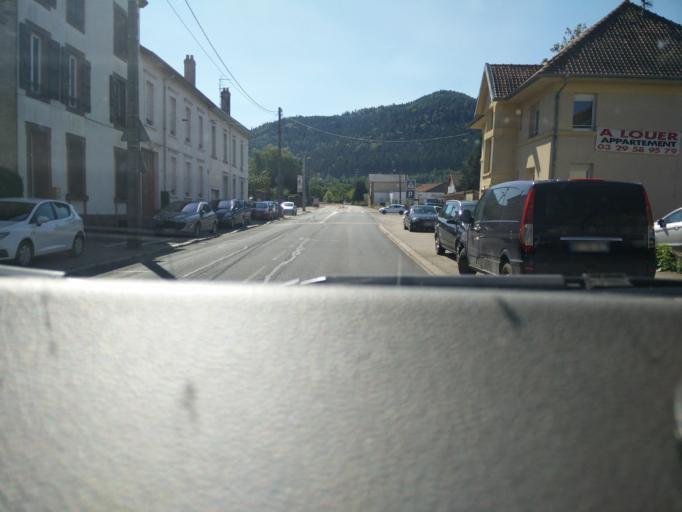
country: FR
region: Lorraine
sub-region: Departement des Vosges
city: Etival-Clairefontaine
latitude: 48.4036
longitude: 6.8471
